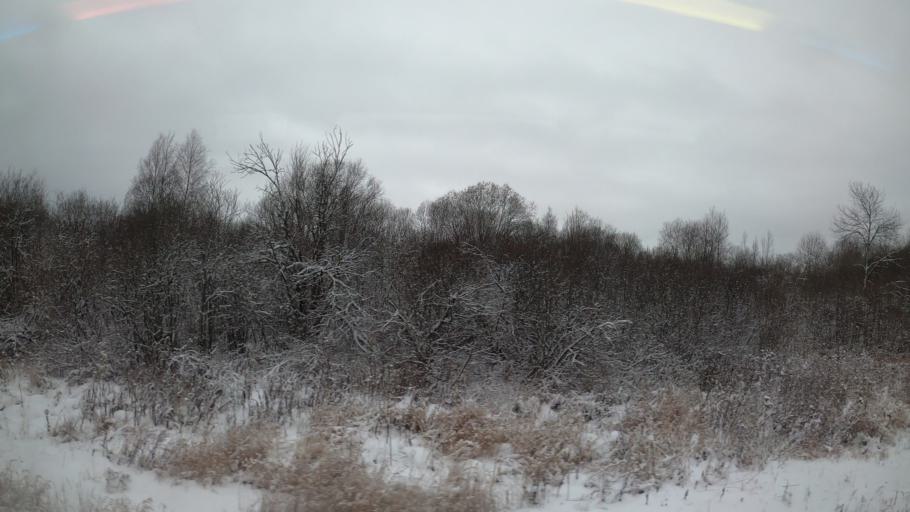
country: RU
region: Jaroslavl
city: Pereslavl'-Zalesskiy
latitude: 56.7084
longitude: 38.9110
